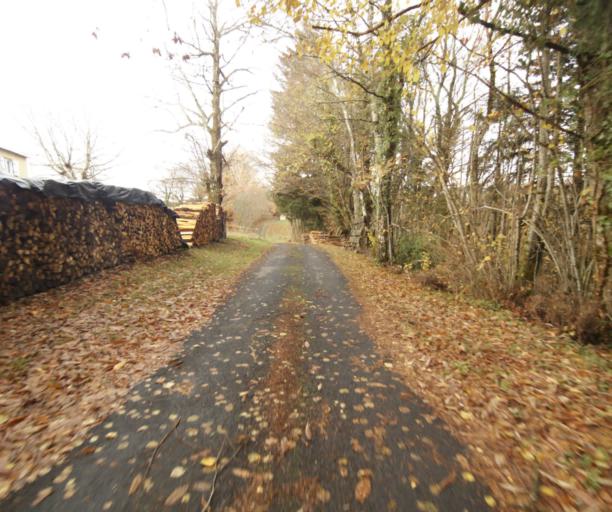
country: FR
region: Limousin
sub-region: Departement de la Correze
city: Cornil
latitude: 45.2055
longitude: 1.7218
